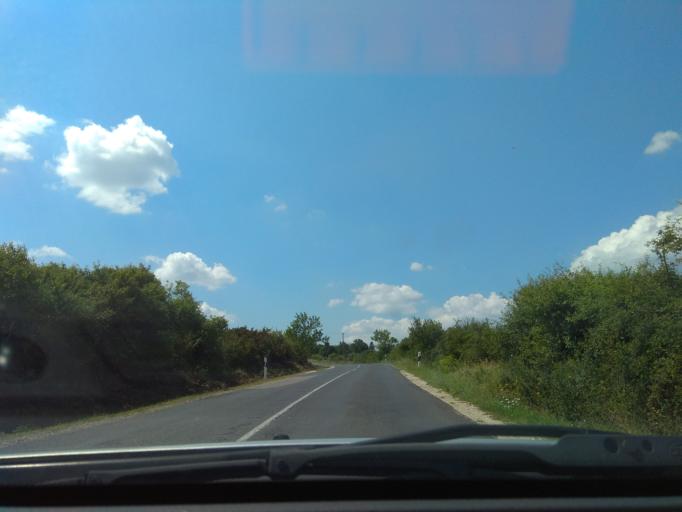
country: HU
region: Borsod-Abauj-Zemplen
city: Malyi
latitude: 48.0395
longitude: 20.7852
